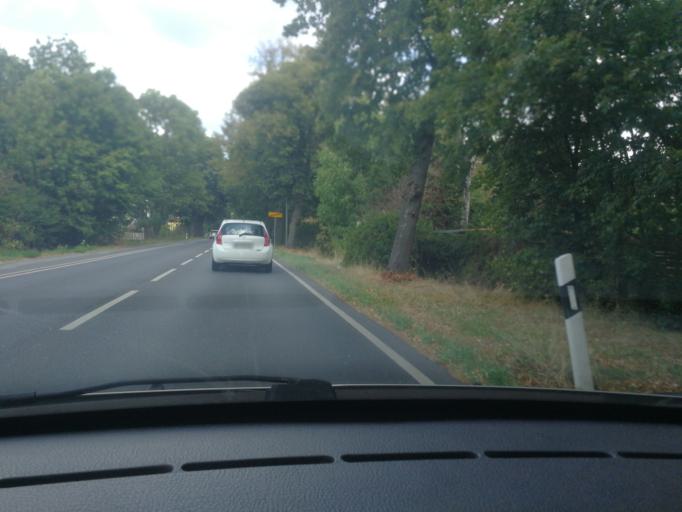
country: DE
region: North Rhine-Westphalia
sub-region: Regierungsbezirk Dusseldorf
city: Moers
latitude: 51.4061
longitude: 6.6606
